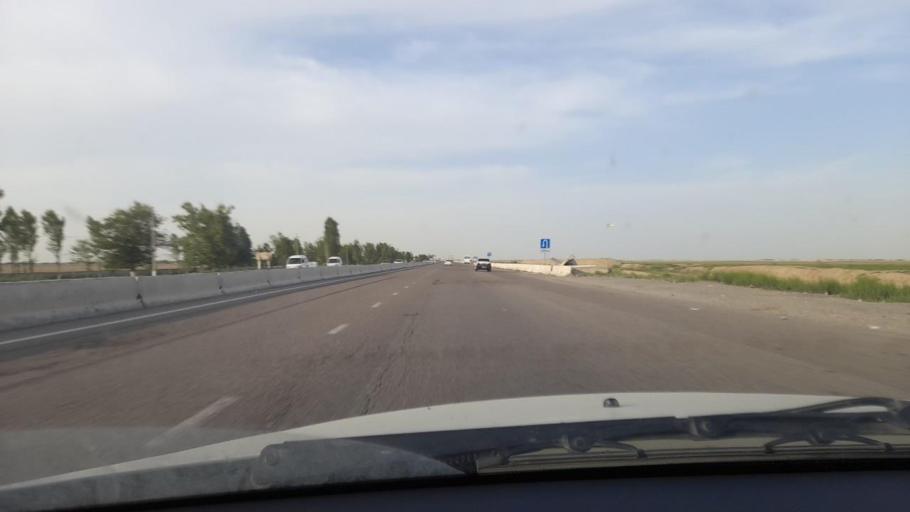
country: UZ
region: Jizzax
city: Dustlik
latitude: 40.4445
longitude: 68.2419
